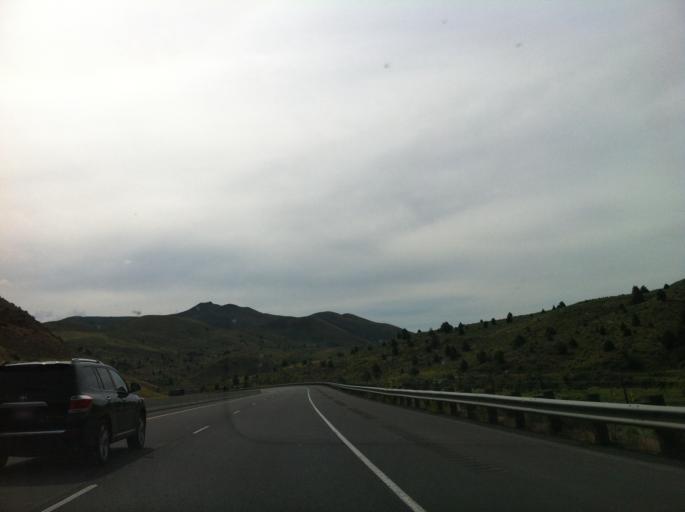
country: US
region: Idaho
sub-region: Washington County
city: Weiser
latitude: 44.5212
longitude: -117.3850
